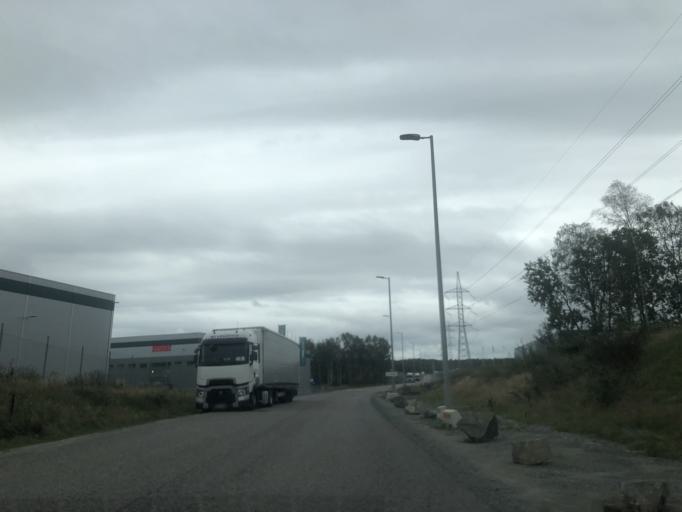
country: SE
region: Vaestra Goetaland
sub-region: Goteborg
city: Majorna
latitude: 57.7372
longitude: 11.8627
